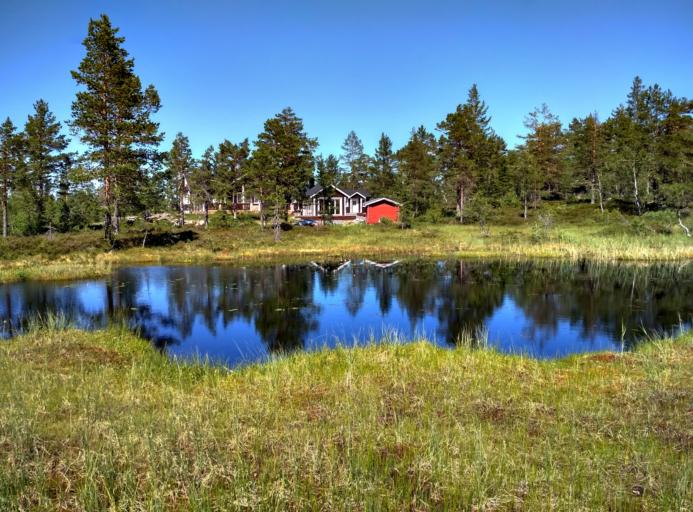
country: NO
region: Buskerud
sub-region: Kongsberg
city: Kongsberg
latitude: 59.5379
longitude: 9.5765
